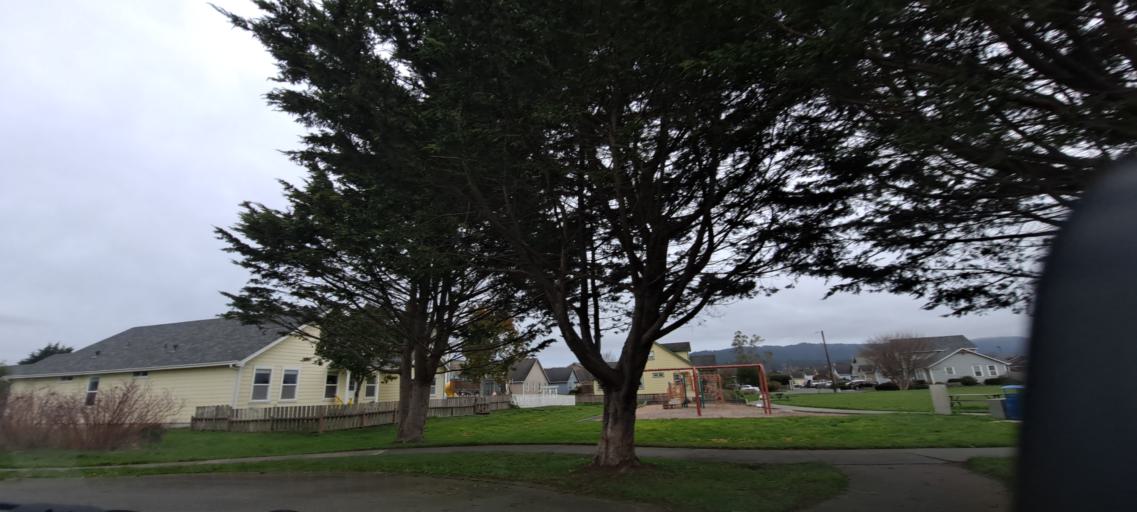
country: US
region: California
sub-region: Humboldt County
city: Arcata
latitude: 40.8712
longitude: -124.1035
